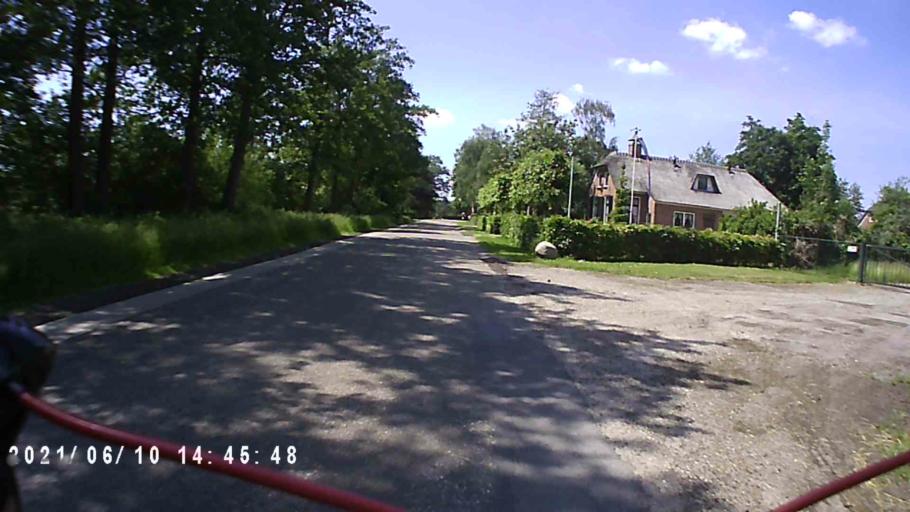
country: NL
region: Groningen
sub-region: Gemeente Grootegast
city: Grootegast
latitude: 53.2365
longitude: 6.2765
